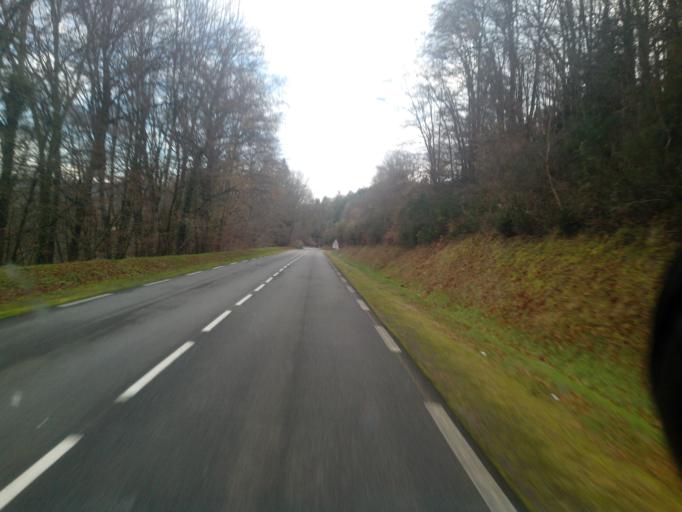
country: FR
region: Limousin
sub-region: Departement de la Haute-Vienne
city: Eymoutiers
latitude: 45.7230
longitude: 1.7570
